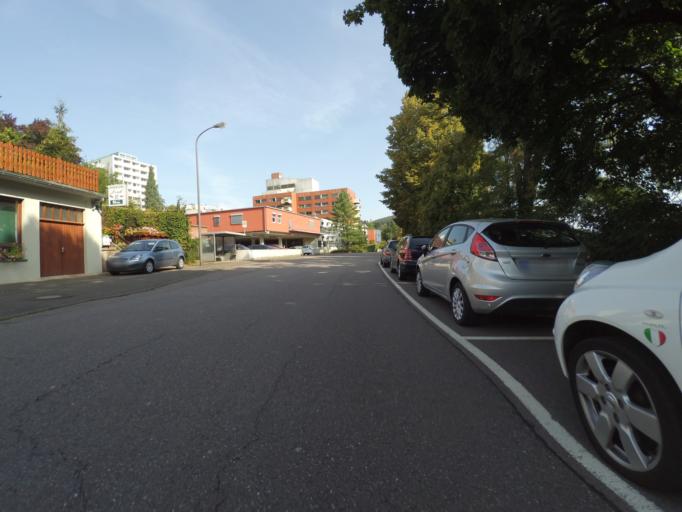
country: DE
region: Rheinland-Pfalz
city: Saarburg
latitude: 49.6015
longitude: 6.5383
